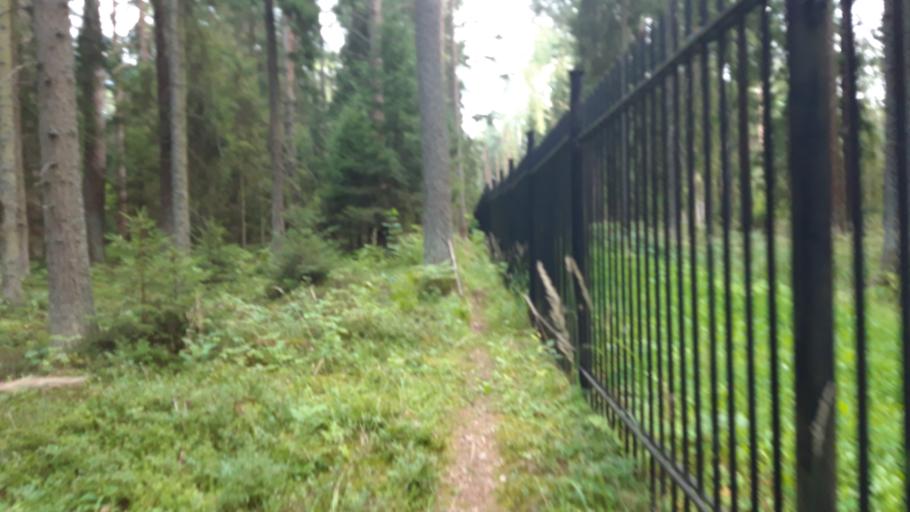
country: RU
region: Tverskaya
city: Konakovo
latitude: 56.6927
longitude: 36.7211
